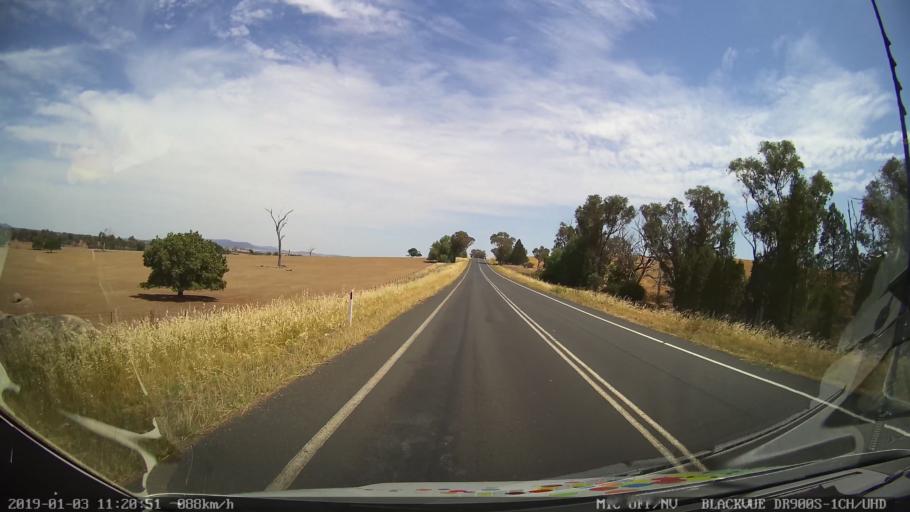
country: AU
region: New South Wales
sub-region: Weddin
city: Grenfell
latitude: -34.0959
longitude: 148.2532
